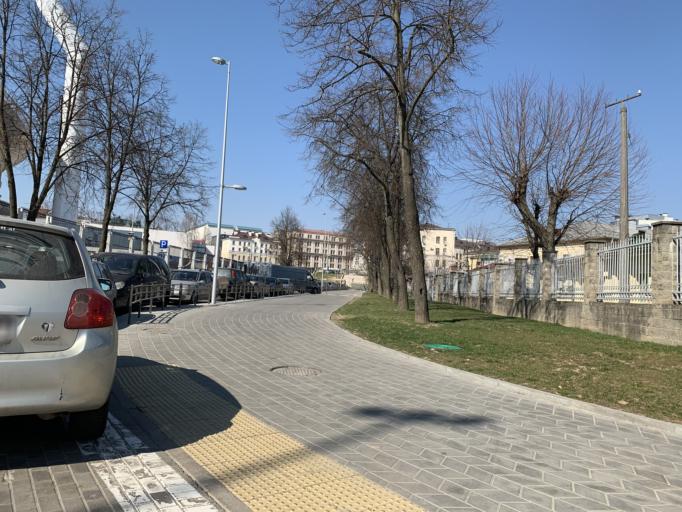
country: BY
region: Minsk
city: Minsk
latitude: 53.8955
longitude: 27.5622
